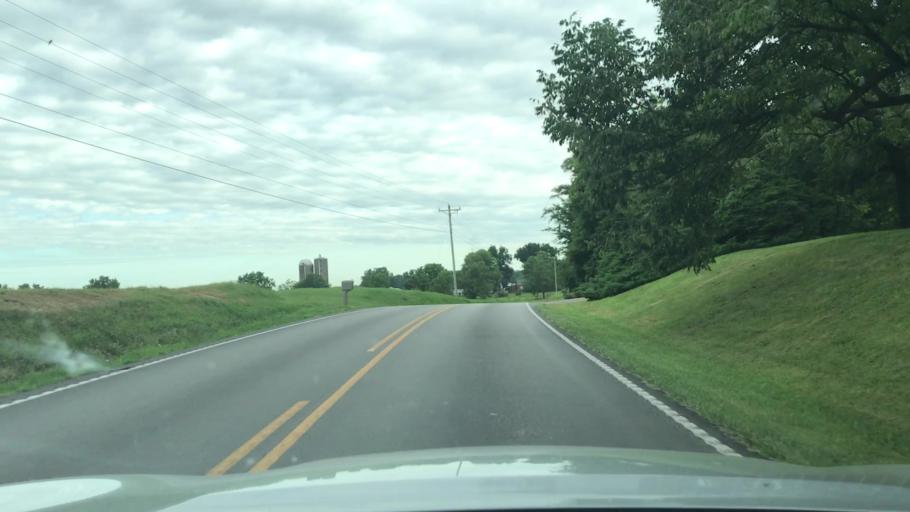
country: US
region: Kentucky
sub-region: Todd County
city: Guthrie
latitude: 36.6920
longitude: -87.2011
